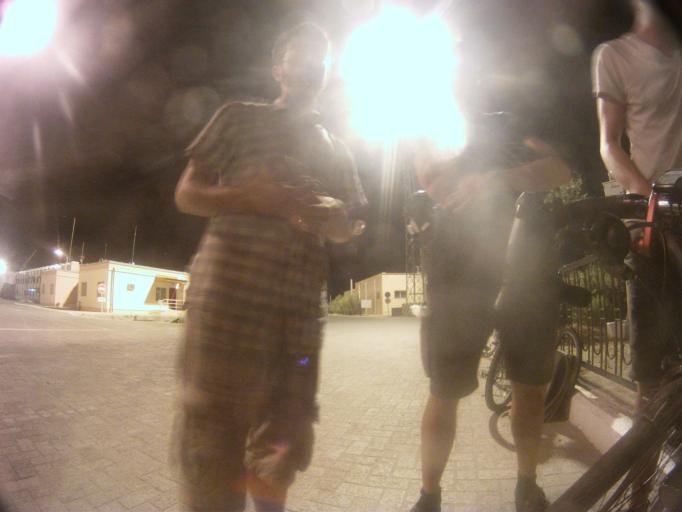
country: KZ
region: Mangghystau
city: Omirzaq
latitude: 43.6031
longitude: 51.2200
